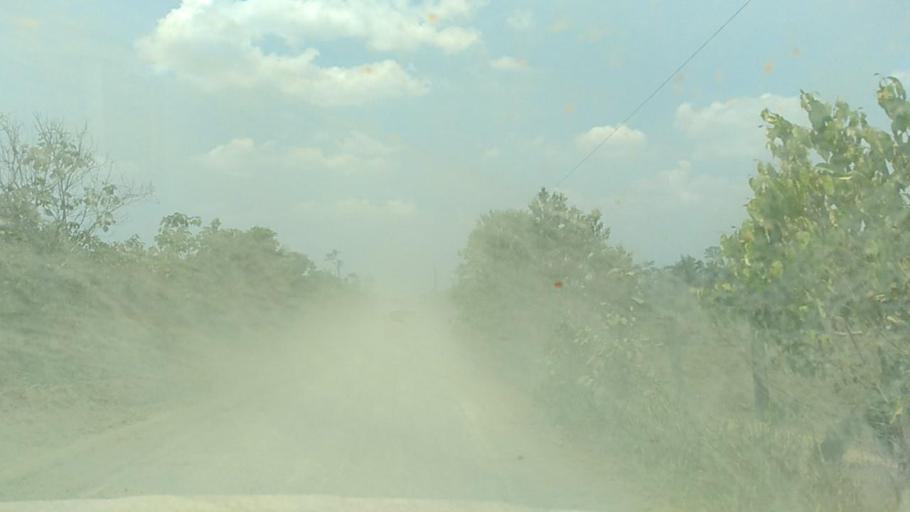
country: BR
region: Rondonia
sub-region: Porto Velho
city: Porto Velho
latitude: -8.7293
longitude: -63.3000
